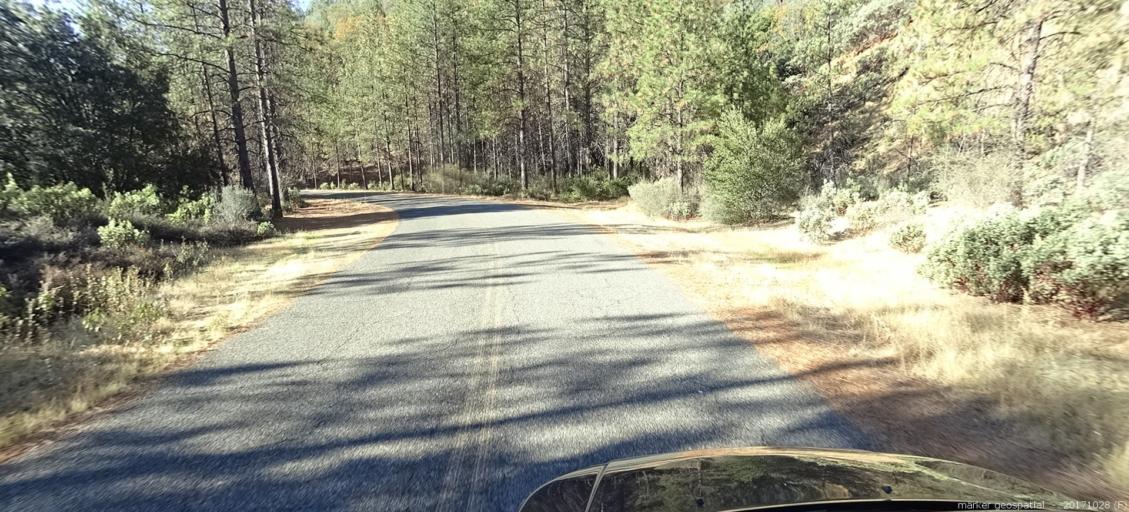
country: US
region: California
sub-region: Trinity County
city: Lewiston
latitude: 40.6639
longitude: -122.6588
